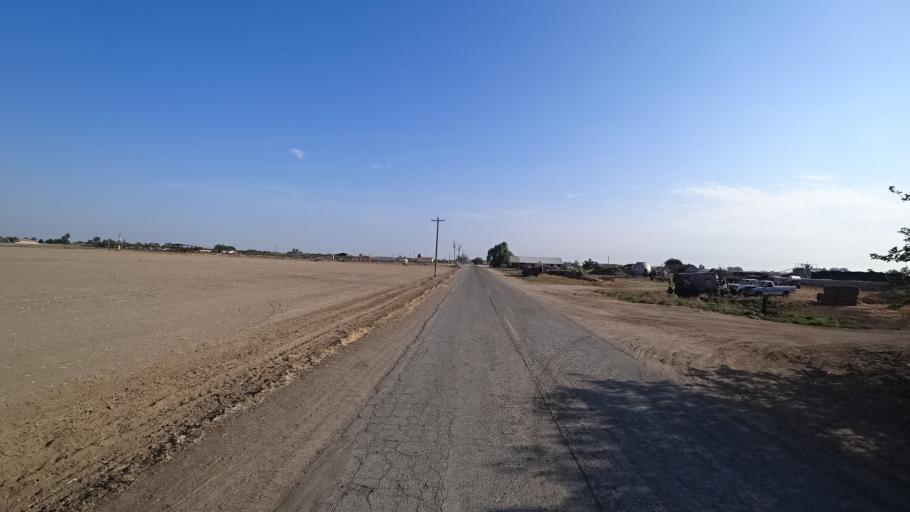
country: US
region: California
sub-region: Fresno County
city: Riverdale
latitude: 36.3769
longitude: -119.8431
